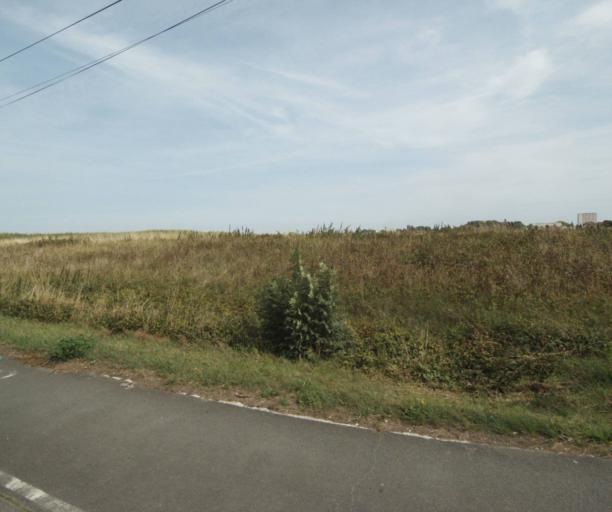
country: FR
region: Nord-Pas-de-Calais
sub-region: Departement du Nord
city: Wattignies
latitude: 50.5955
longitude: 3.0374
